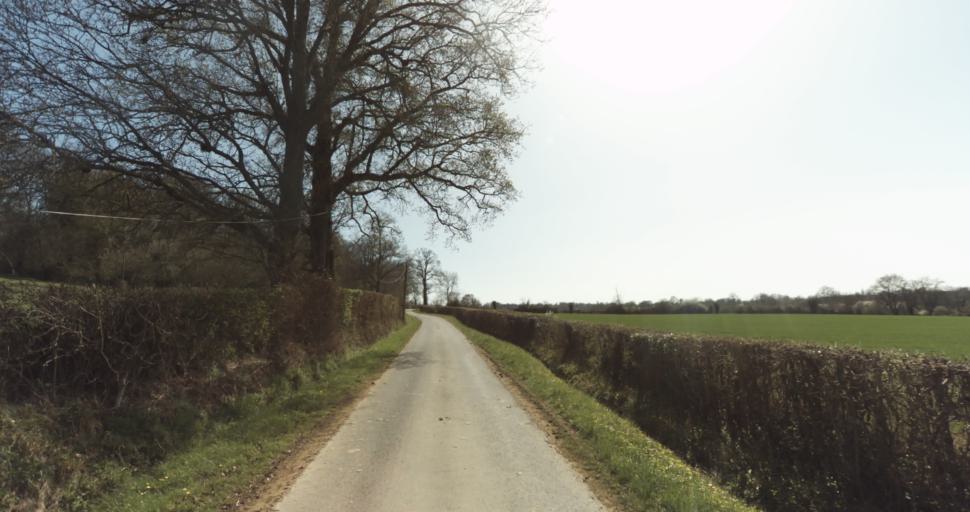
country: FR
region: Lower Normandy
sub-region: Departement du Calvados
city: Saint-Pierre-sur-Dives
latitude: 48.9552
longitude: -0.0028
